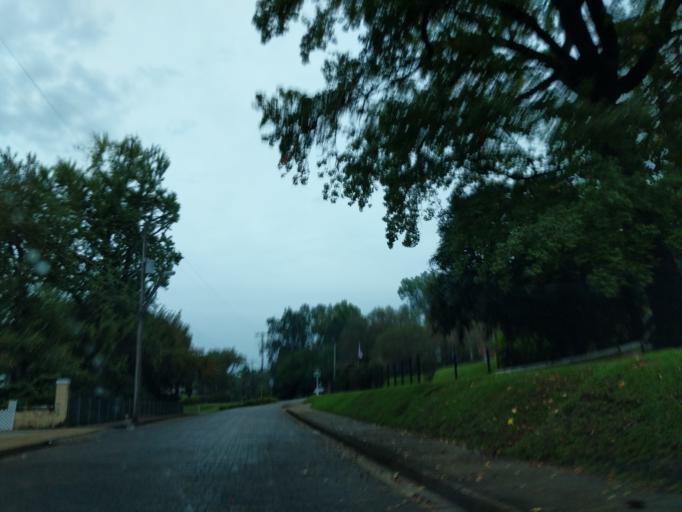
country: US
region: Mississippi
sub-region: Warren County
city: Vicksburg
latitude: 32.3407
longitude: -90.8861
